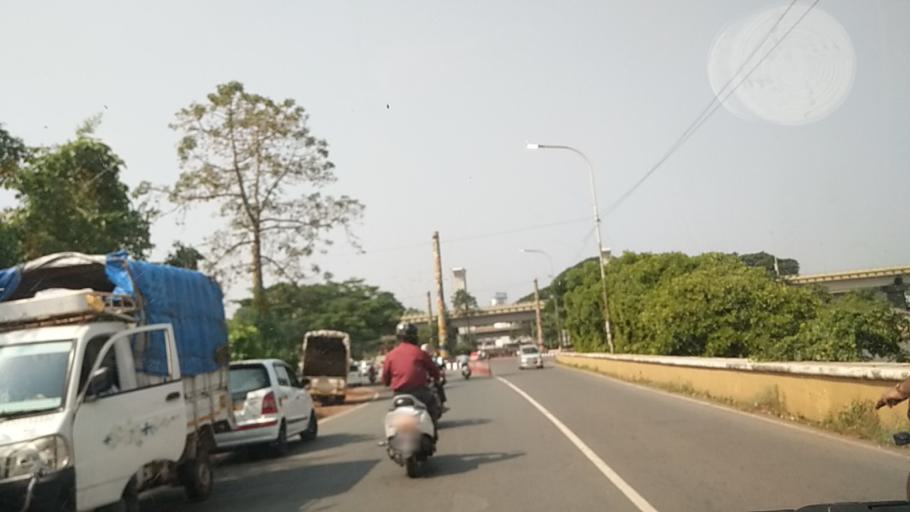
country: IN
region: Goa
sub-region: North Goa
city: Panaji
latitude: 15.4992
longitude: 73.8389
